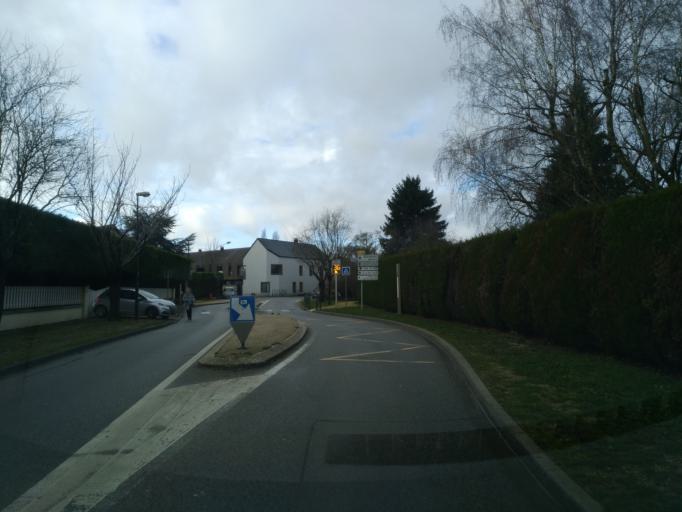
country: FR
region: Ile-de-France
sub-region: Departement des Yvelines
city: Les Alluets-le-Roi
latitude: 48.9133
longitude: 1.9229
